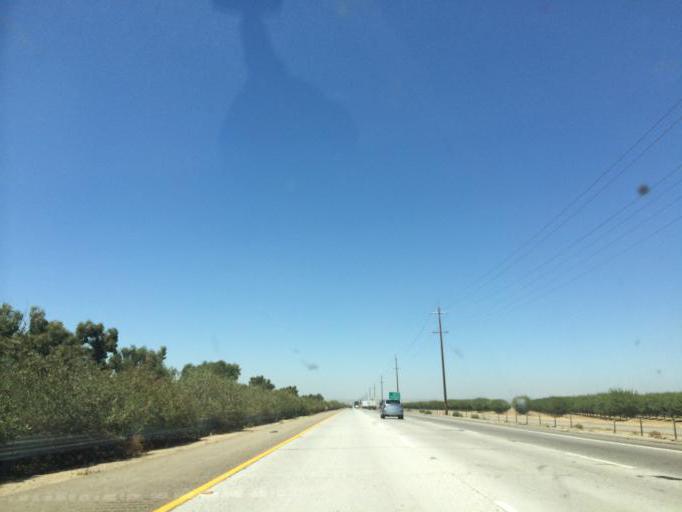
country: US
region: California
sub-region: Kern County
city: Weedpatch
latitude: 35.0421
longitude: -118.9628
